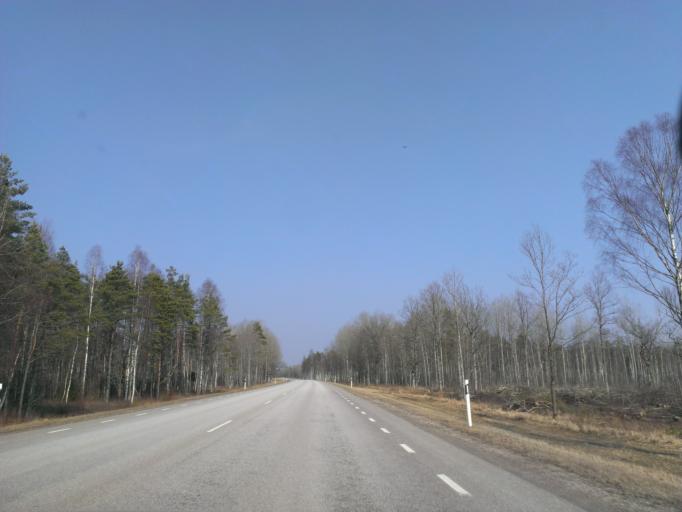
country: EE
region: Saare
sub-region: Orissaare vald
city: Orissaare
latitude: 58.4539
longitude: 22.8051
